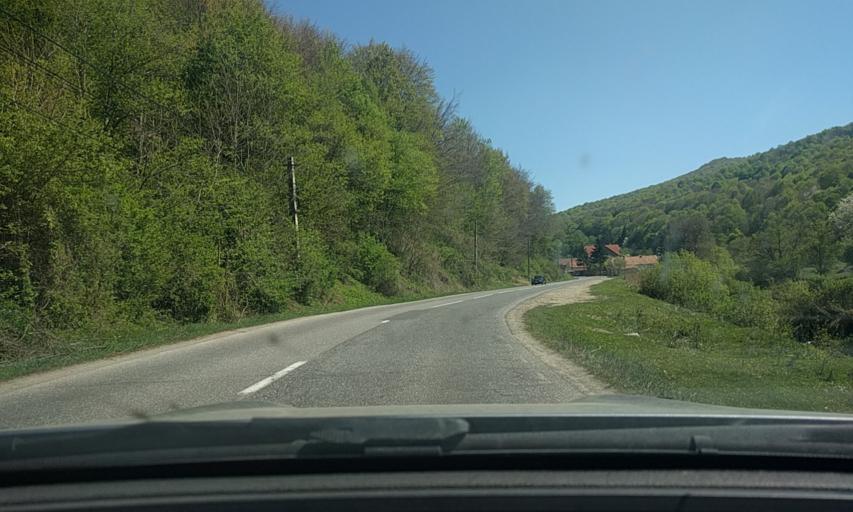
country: RO
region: Brasov
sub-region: Comuna Teliu
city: Teliu
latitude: 45.6855
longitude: 25.9000
